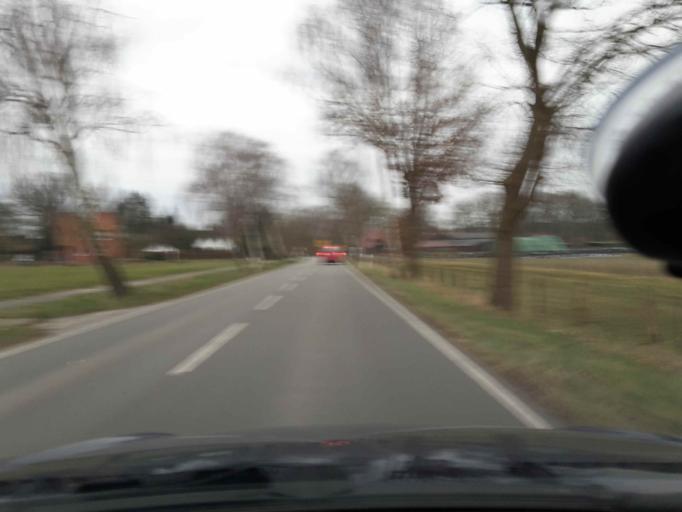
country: DE
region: Lower Saxony
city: Hanstedt
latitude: 53.2397
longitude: 10.0270
